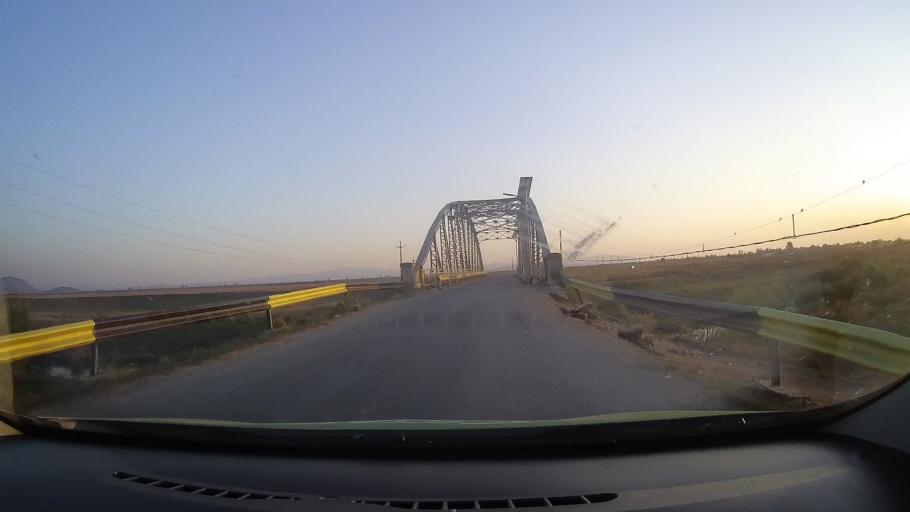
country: RO
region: Arad
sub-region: Comuna Sicula
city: Sicula
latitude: 46.4308
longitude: 21.7571
